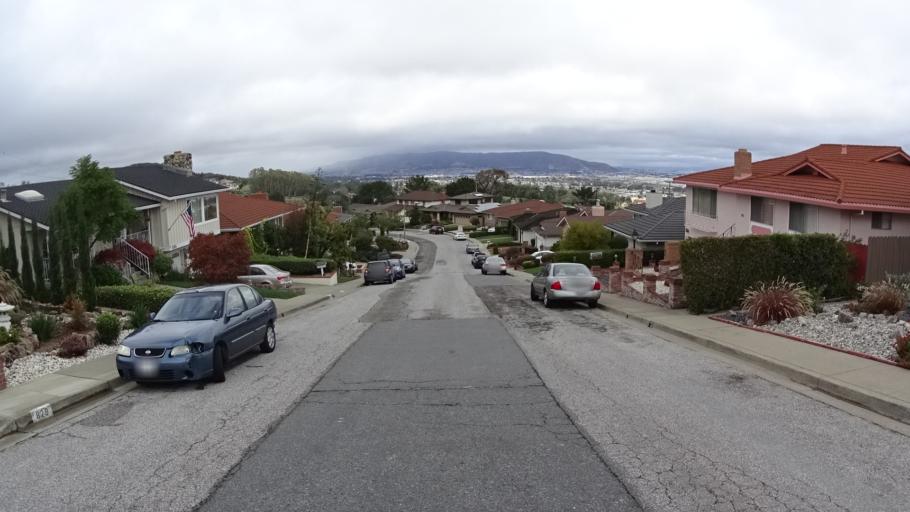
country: US
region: California
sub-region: San Mateo County
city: Millbrae
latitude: 37.5973
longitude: -122.4106
